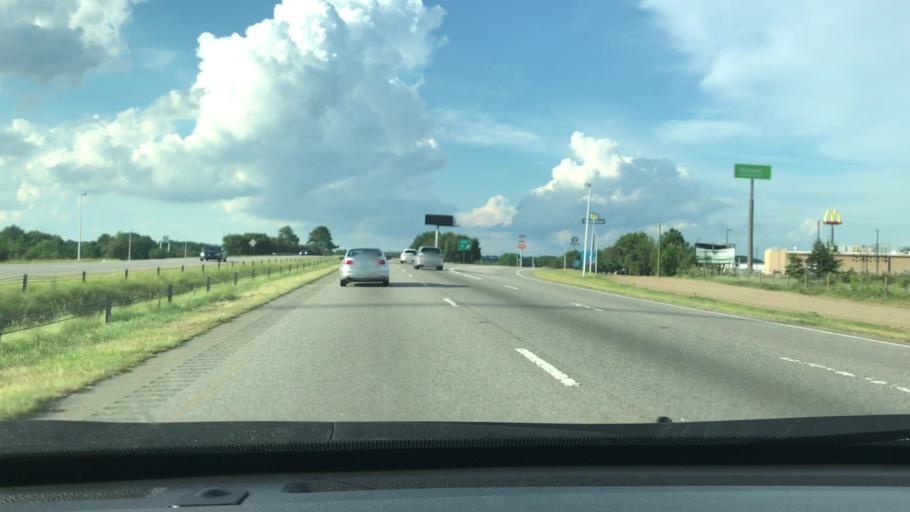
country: US
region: North Carolina
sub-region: Robeson County
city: Saint Pauls
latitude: 34.8074
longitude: -78.9878
